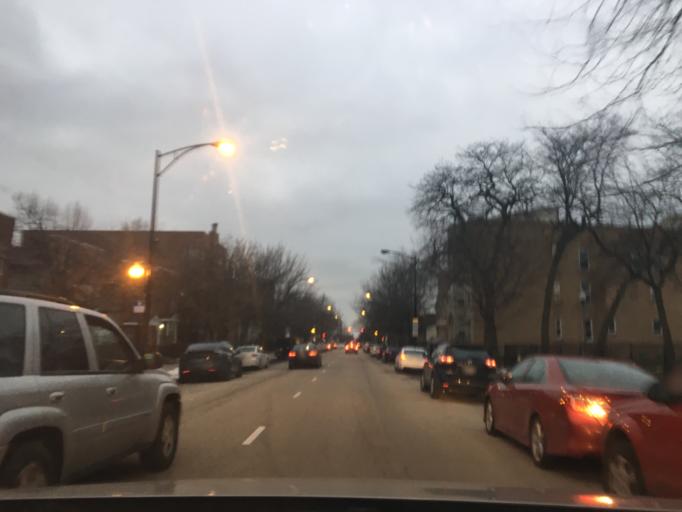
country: US
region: Illinois
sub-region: Cook County
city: Chicago
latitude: 41.8831
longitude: -87.6841
